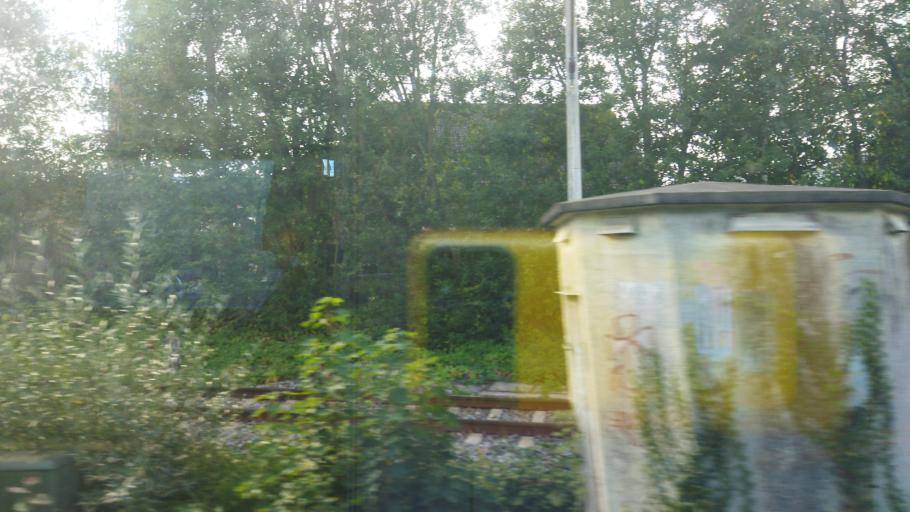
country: DE
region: Lower Saxony
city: Emden
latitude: 53.3629
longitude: 7.1993
